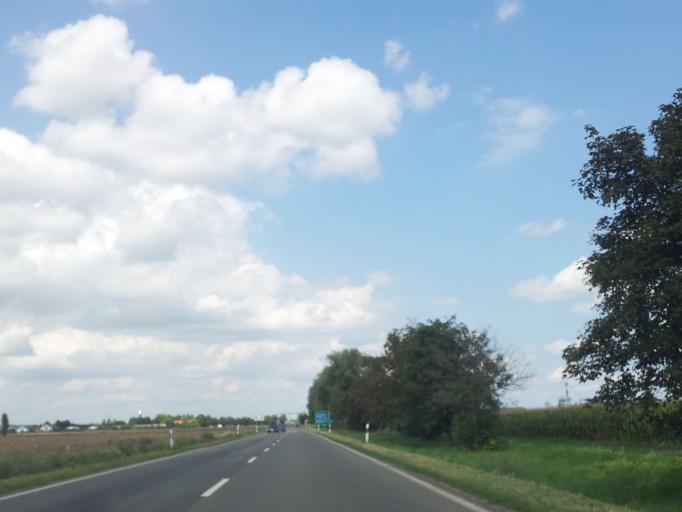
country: HU
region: Baranya
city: Mohacs
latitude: 45.9677
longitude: 18.6726
